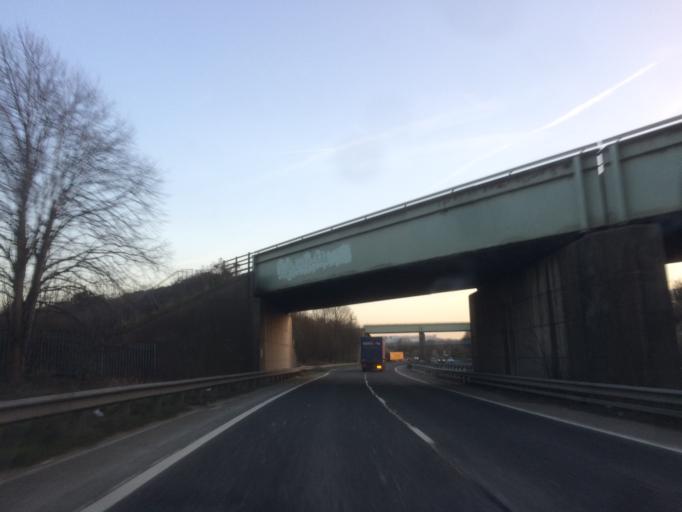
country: GB
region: England
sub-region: City and Borough of Wakefield
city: Ferrybridge
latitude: 53.7082
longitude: -1.2690
